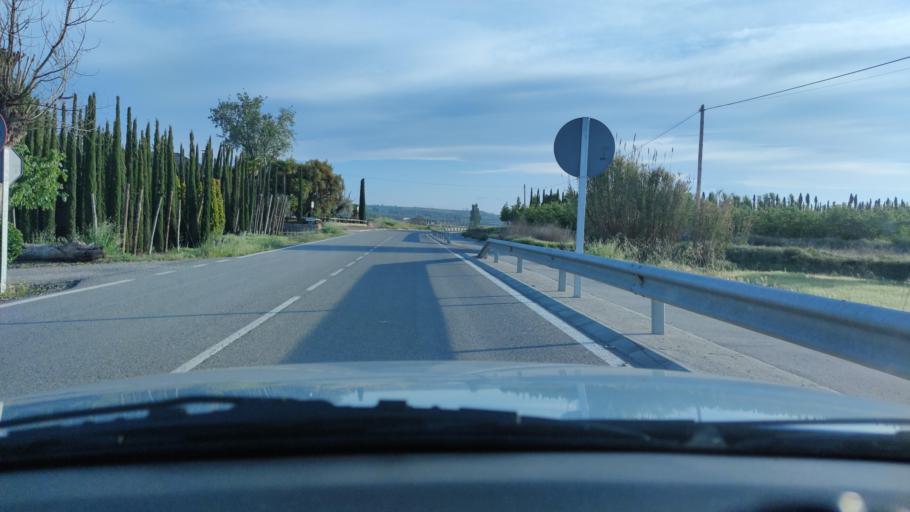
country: ES
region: Catalonia
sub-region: Provincia de Lleida
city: Castellsera
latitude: 41.7493
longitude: 0.9912
